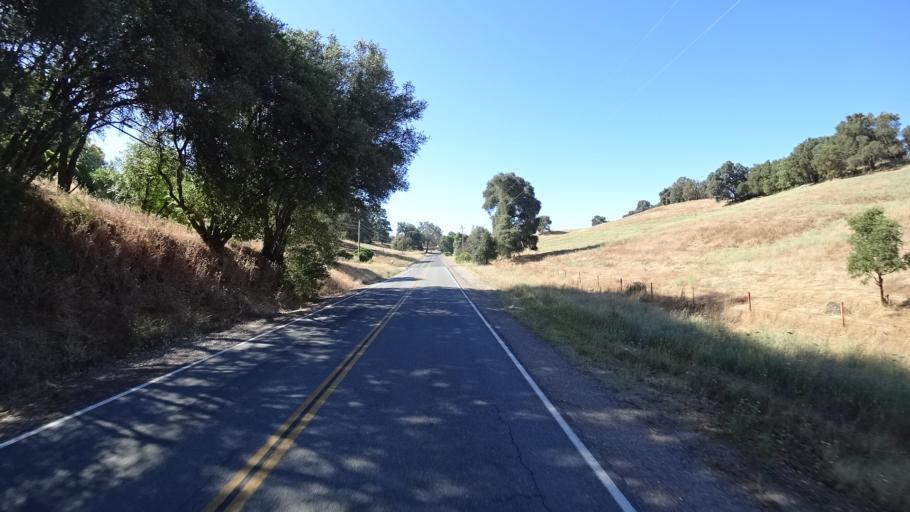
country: US
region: California
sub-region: Calaveras County
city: San Andreas
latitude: 38.2105
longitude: -120.6846
